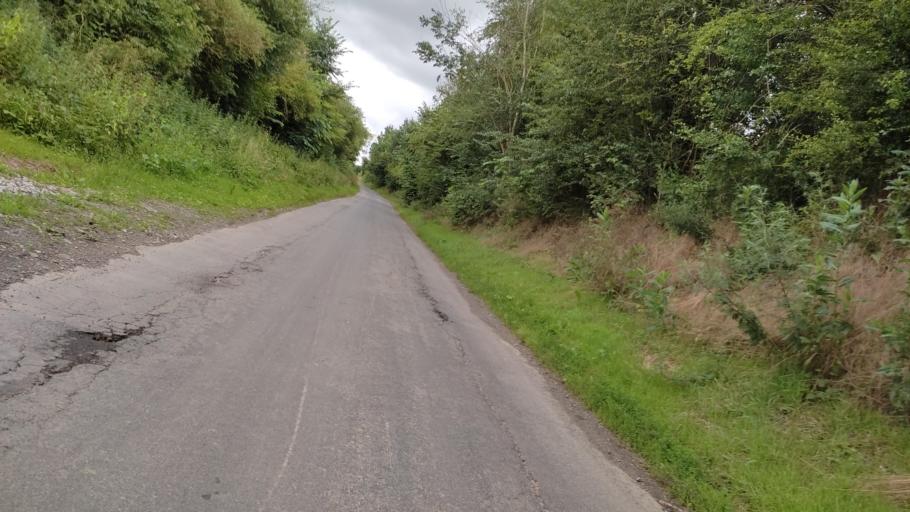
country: FR
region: Nord-Pas-de-Calais
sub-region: Departement du Pas-de-Calais
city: Dainville
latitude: 50.2769
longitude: 2.7144
